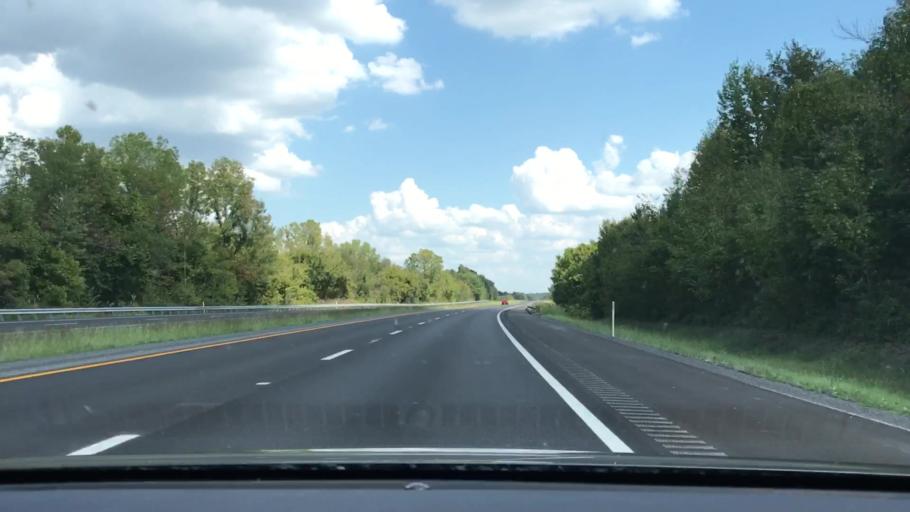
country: US
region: Kentucky
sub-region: Lyon County
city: Eddyville
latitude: 37.0832
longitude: -88.0695
